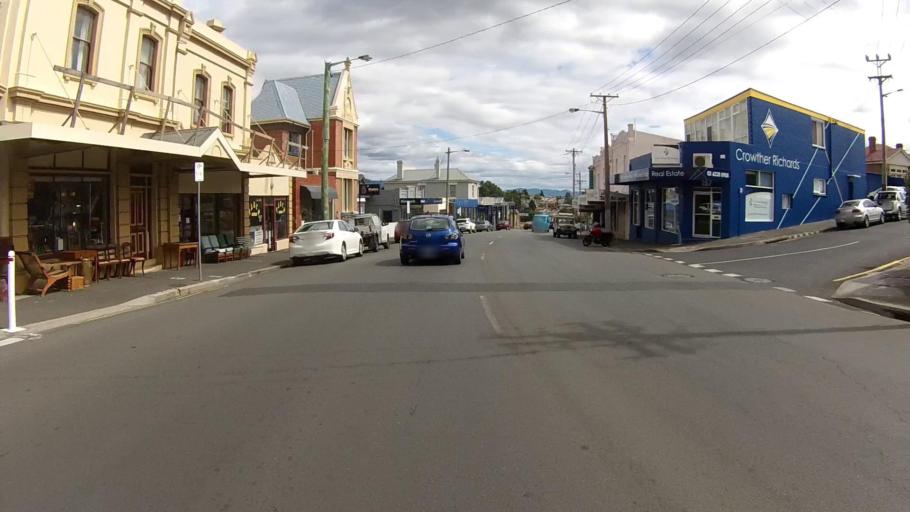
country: AU
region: Tasmania
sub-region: Hobart
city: New Town
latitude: -42.8589
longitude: 147.3048
